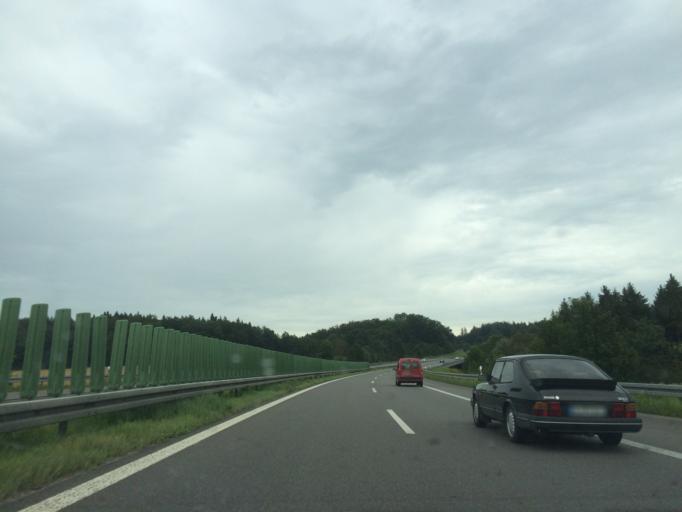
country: DE
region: Baden-Wuerttemberg
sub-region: Tuebingen Region
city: Baindt
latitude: 47.8633
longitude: 9.6568
